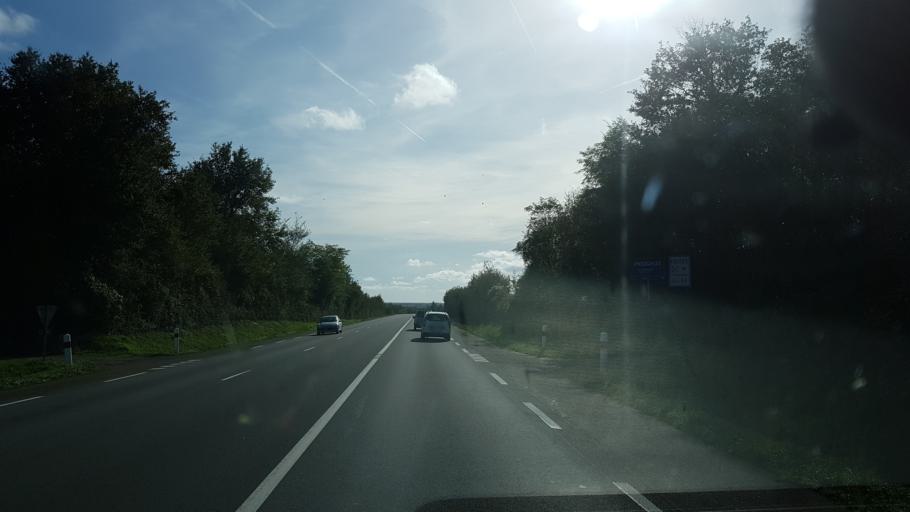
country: FR
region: Poitou-Charentes
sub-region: Departement de la Charente
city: Chasseneuil-sur-Bonnieure
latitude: 45.8507
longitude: 0.4626
